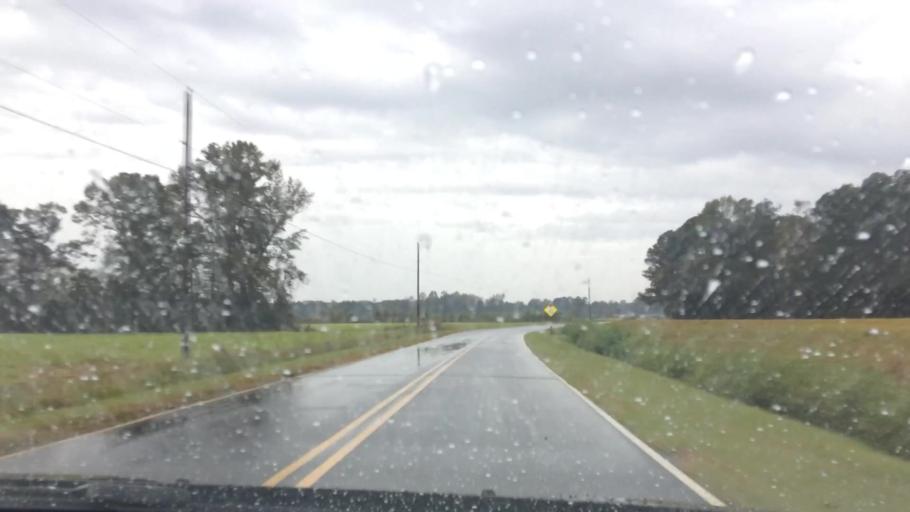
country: US
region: North Carolina
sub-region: Pitt County
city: Grifton
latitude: 35.3836
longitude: -77.4116
